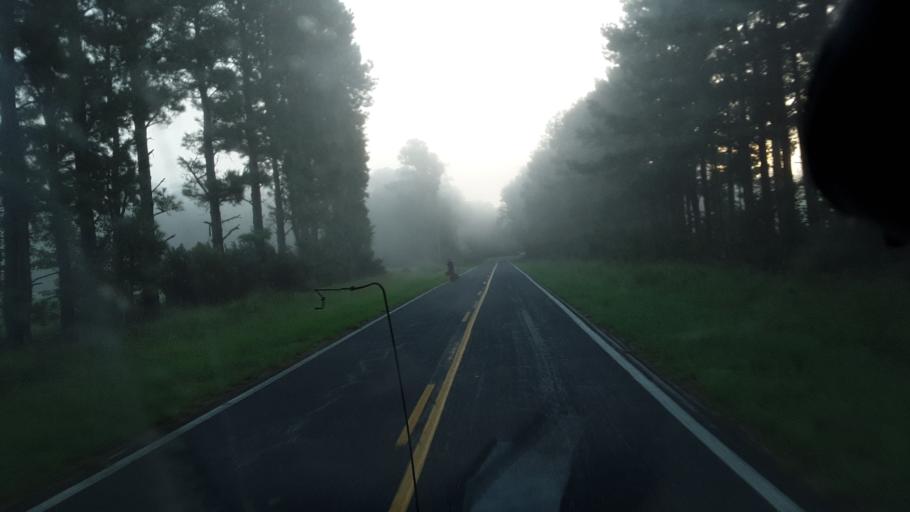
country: US
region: South Carolina
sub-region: Clarendon County
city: Manning
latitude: 33.7278
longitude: -80.1107
